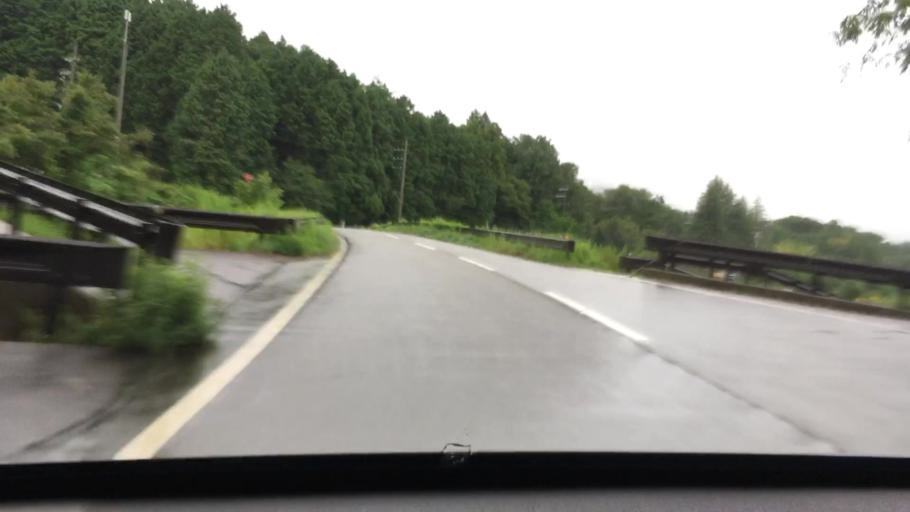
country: JP
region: Hyogo
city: Toyooka
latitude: 35.3097
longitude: 134.8737
